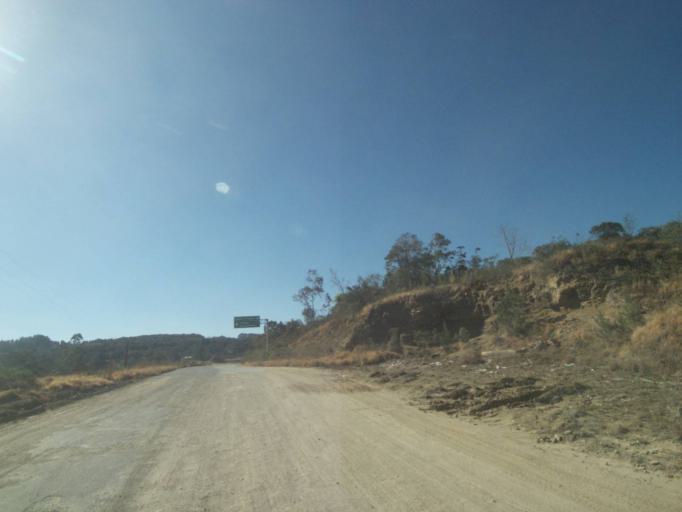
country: BR
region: Parana
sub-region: Tibagi
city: Tibagi
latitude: -24.8194
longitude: -50.4895
